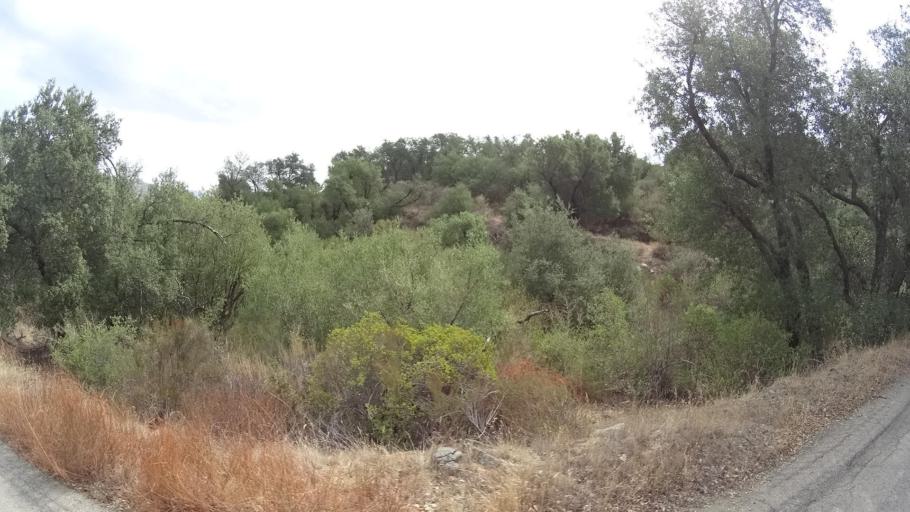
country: US
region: California
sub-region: San Diego County
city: San Diego Country Estates
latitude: 33.1052
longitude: -116.7904
